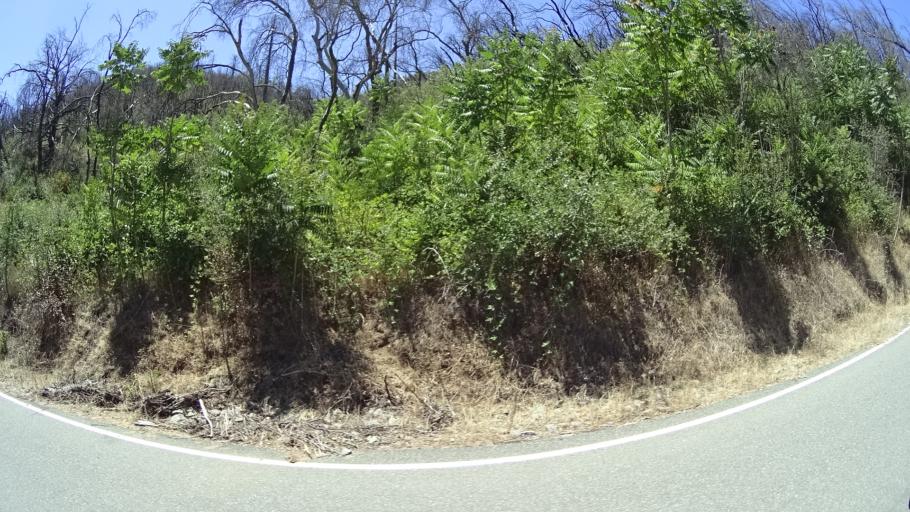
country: US
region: California
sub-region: Calaveras County
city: San Andreas
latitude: 38.2904
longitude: -120.6712
